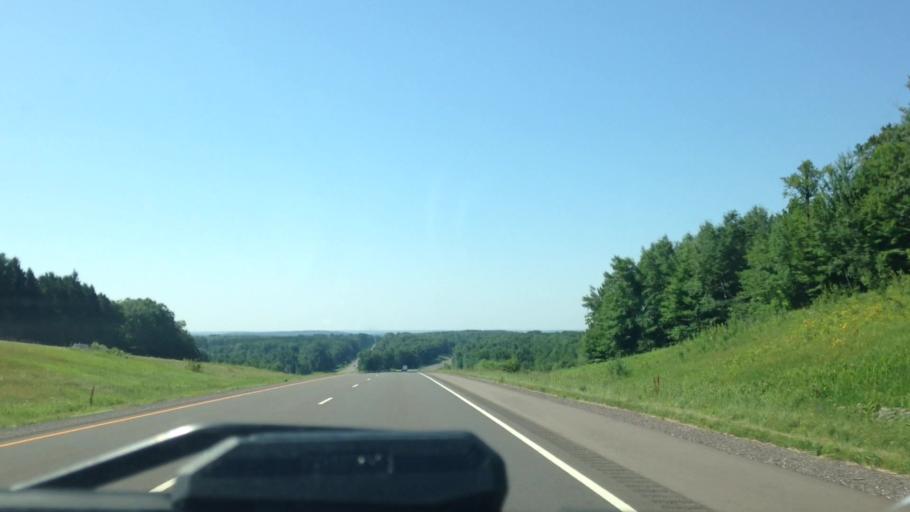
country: US
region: Wisconsin
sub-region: Washburn County
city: Spooner
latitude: 45.9563
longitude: -91.8284
